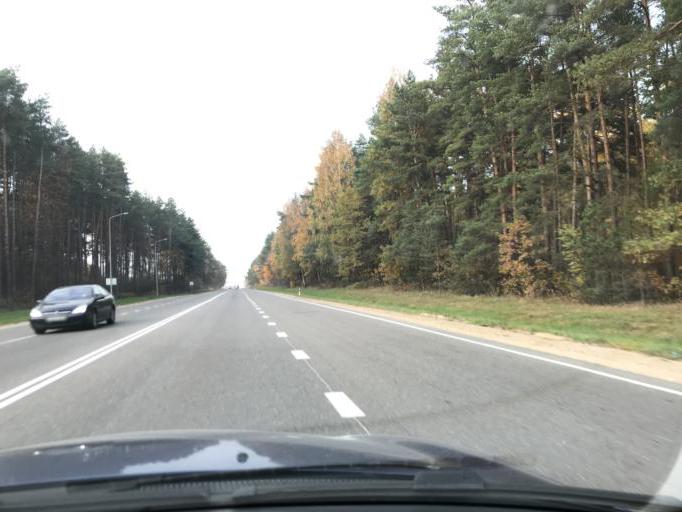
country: BY
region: Grodnenskaya
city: Lida
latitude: 53.8383
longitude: 25.3465
